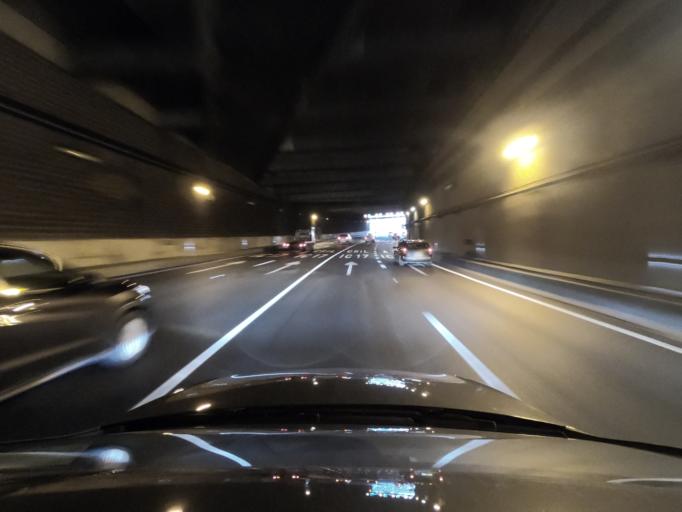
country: PT
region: Lisbon
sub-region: Odivelas
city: Pontinha
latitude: 38.7435
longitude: -9.2058
